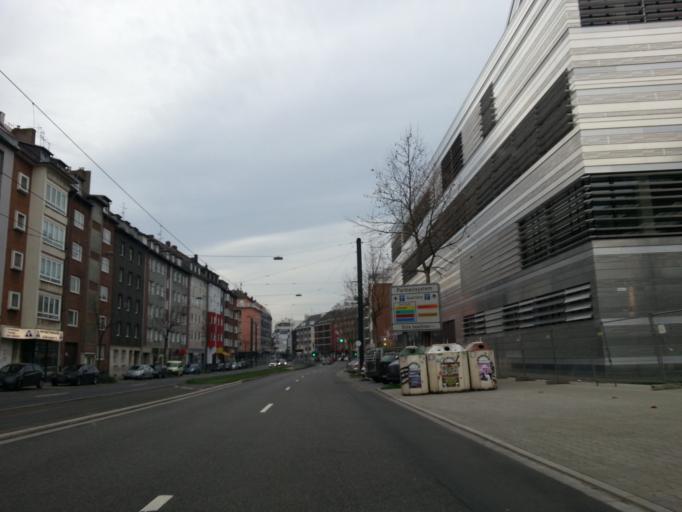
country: DE
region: North Rhine-Westphalia
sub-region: Regierungsbezirk Dusseldorf
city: Dusseldorf
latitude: 51.2464
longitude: 6.7917
